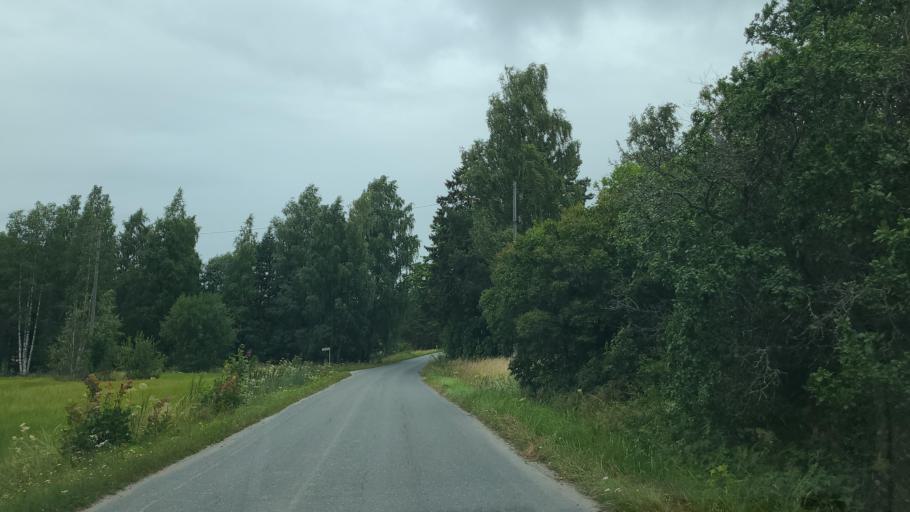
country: FI
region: Varsinais-Suomi
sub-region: Aboland-Turunmaa
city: Dragsfjaerd
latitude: 60.0744
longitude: 22.4499
